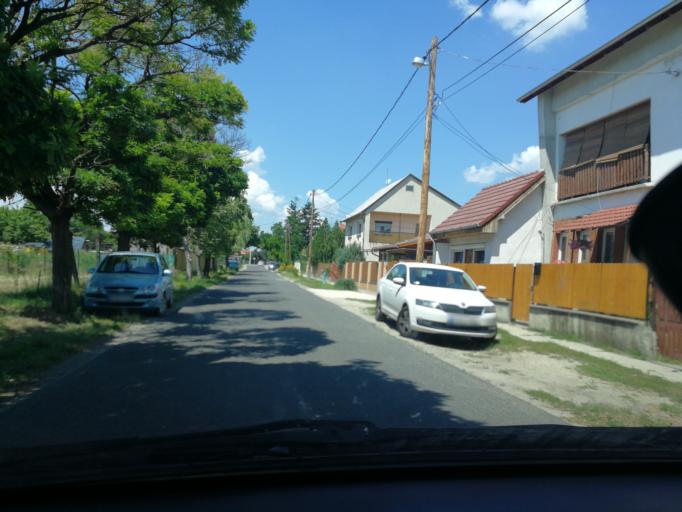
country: HU
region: Pest
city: Halasztelek
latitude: 47.3565
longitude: 18.9873
